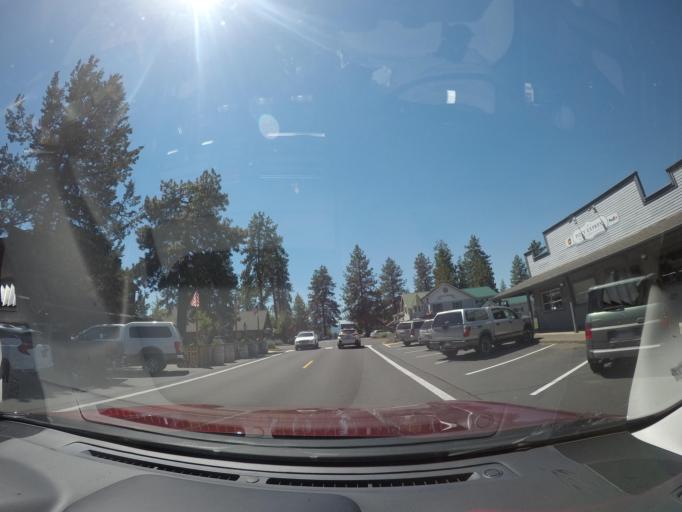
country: US
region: Oregon
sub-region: Deschutes County
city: Sisters
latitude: 44.2905
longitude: -121.5519
